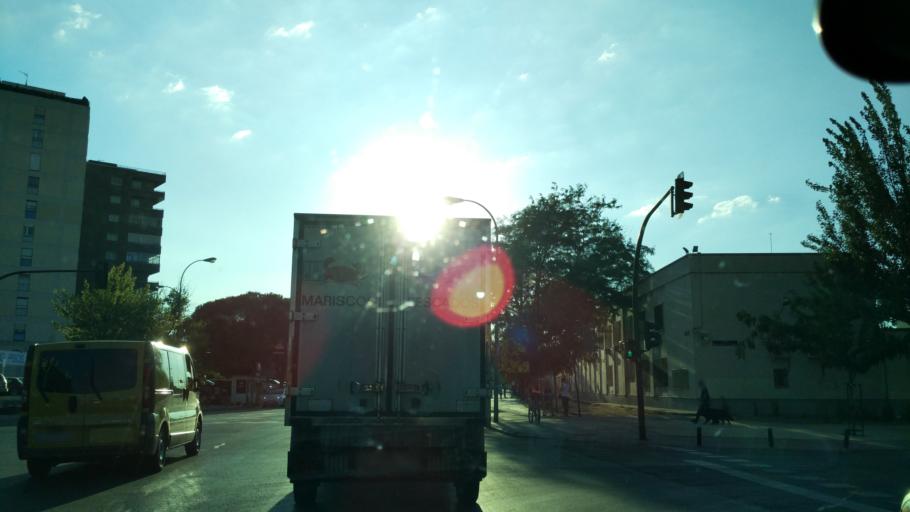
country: ES
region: Madrid
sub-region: Provincia de Madrid
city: Tetuan de las Victorias
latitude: 40.4578
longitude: -3.7129
